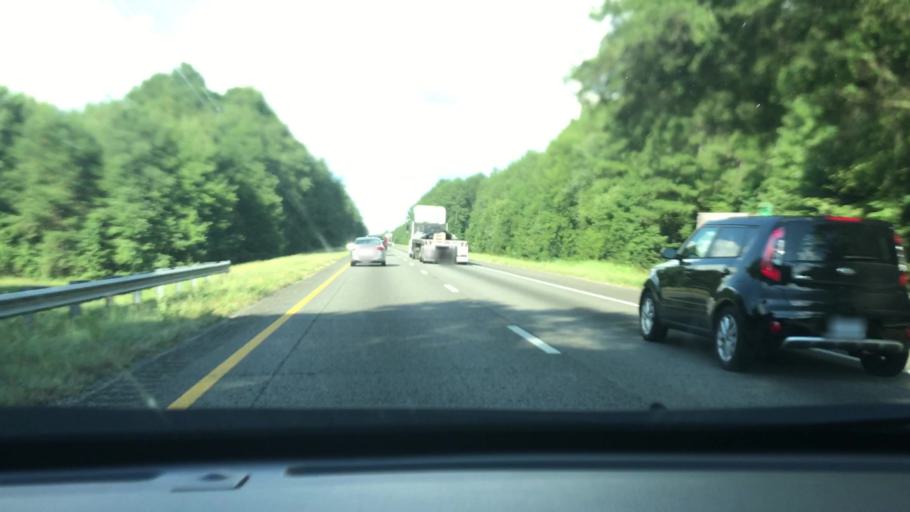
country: US
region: South Carolina
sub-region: Dillon County
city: Latta
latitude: 34.3138
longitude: -79.6040
